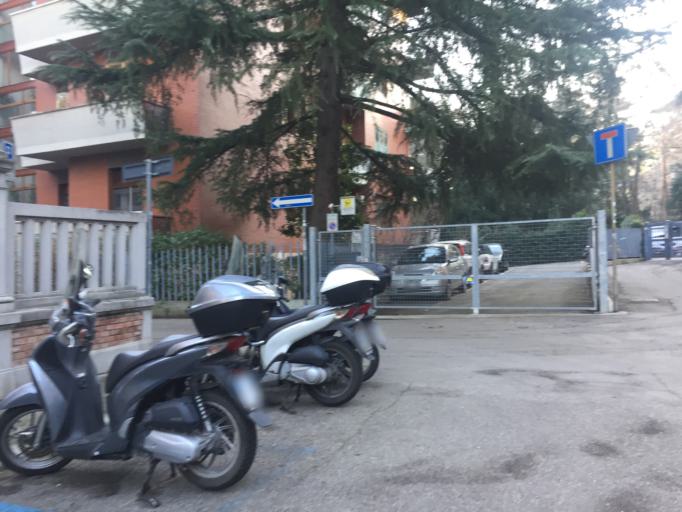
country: IT
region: Emilia-Romagna
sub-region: Provincia di Bologna
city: Bologna
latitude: 44.4911
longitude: 11.3239
